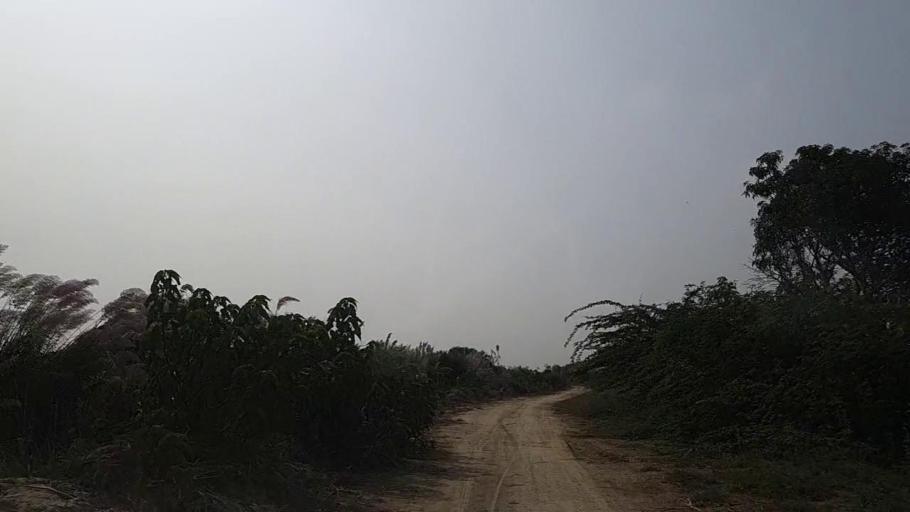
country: PK
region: Sindh
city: Thatta
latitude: 24.6584
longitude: 67.7707
